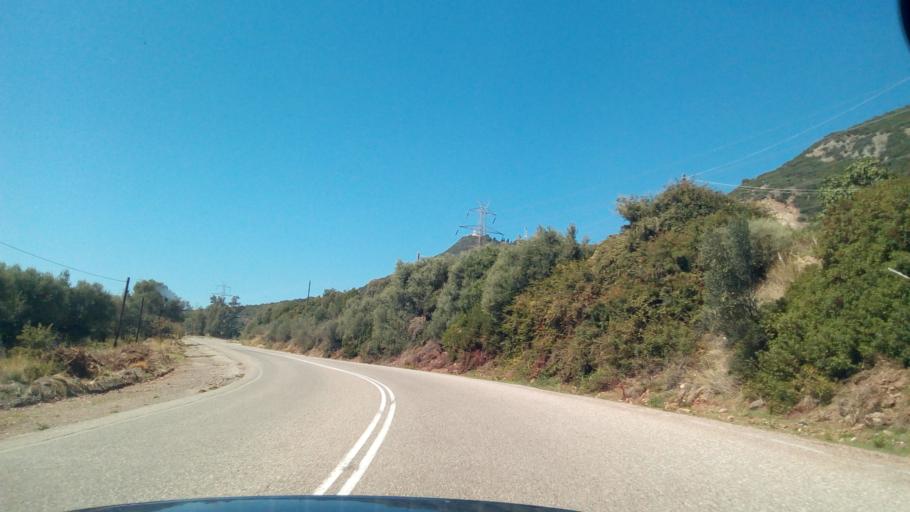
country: GR
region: West Greece
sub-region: Nomos Achaias
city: Kamarai
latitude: 38.4024
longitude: 21.9888
